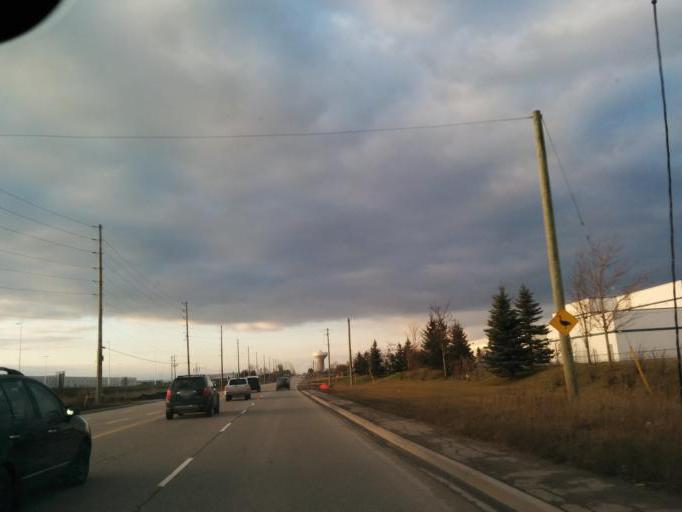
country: CA
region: Ontario
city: Brampton
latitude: 43.8600
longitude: -79.7347
